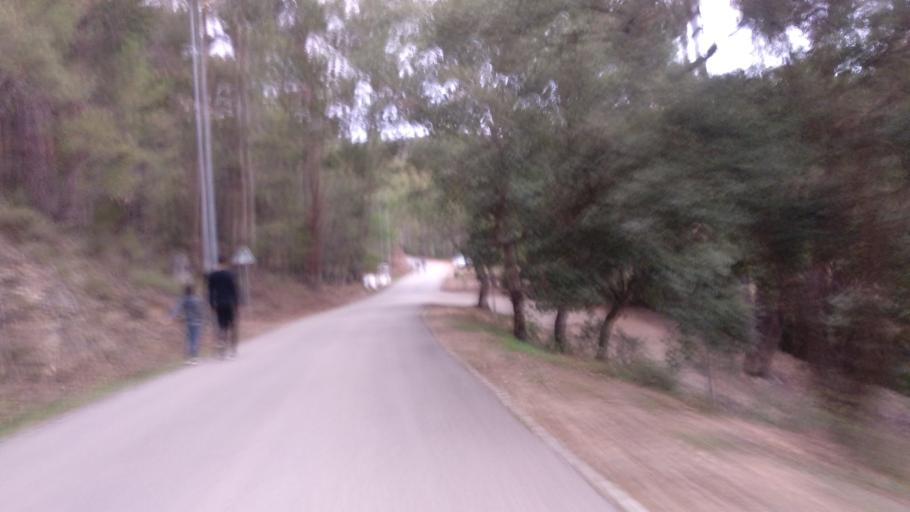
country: PT
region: Faro
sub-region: Sao Bras de Alportel
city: Sao Bras de Alportel
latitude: 37.1830
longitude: -7.9137
